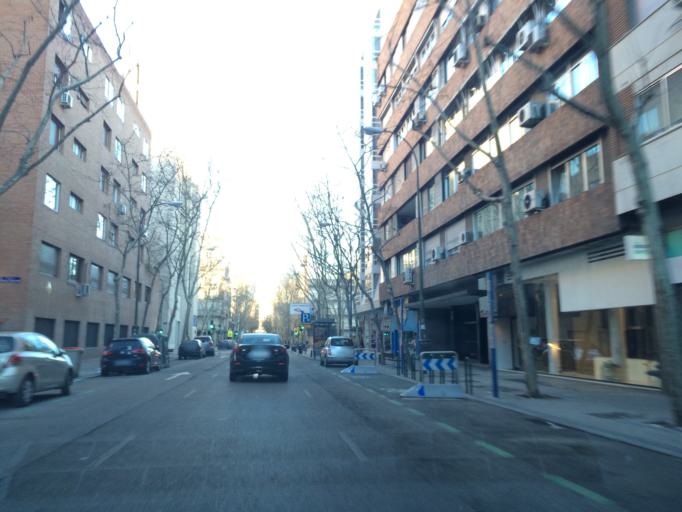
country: ES
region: Madrid
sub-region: Provincia de Madrid
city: Chamberi
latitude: 40.4485
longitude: -3.6969
